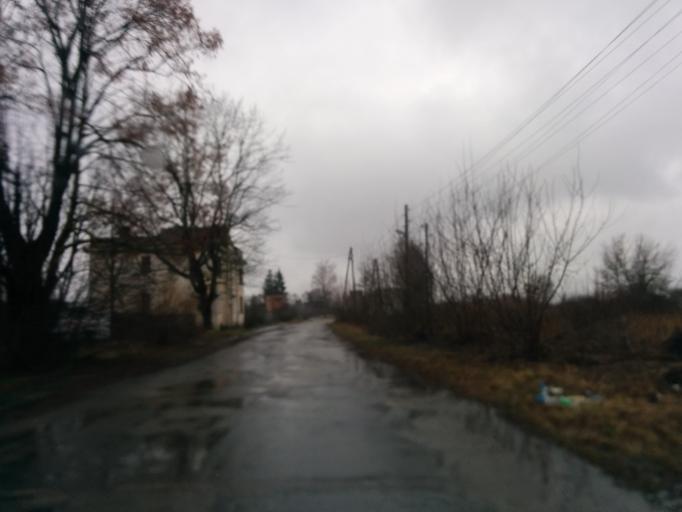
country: LV
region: Jelgava
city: Jelgava
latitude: 56.6627
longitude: 23.7170
